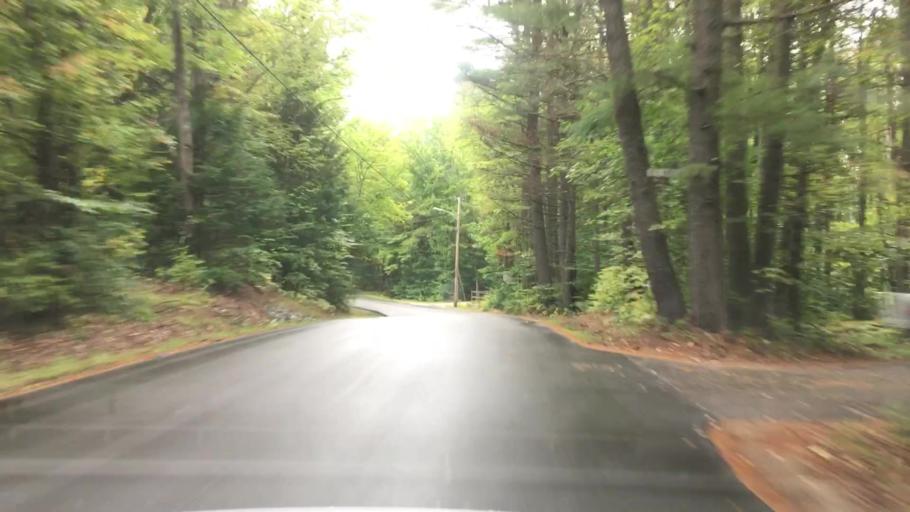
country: US
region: Maine
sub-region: Cumberland County
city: Raymond
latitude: 43.9968
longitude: -70.5675
